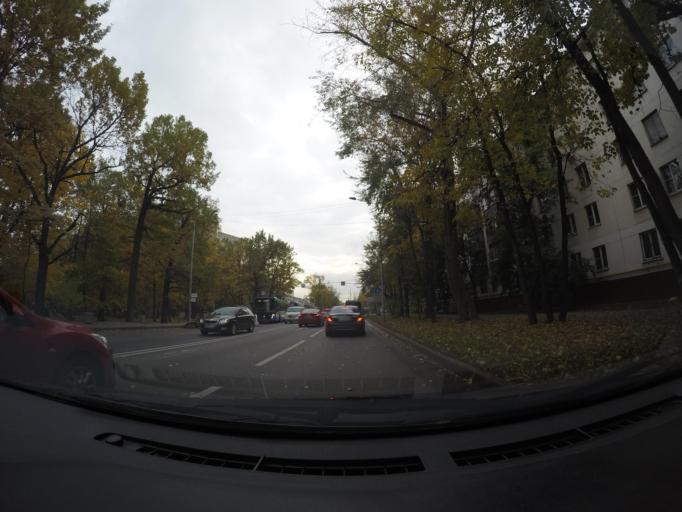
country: RU
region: Moskovskaya
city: Novogireyevo
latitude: 55.7552
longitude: 37.8183
